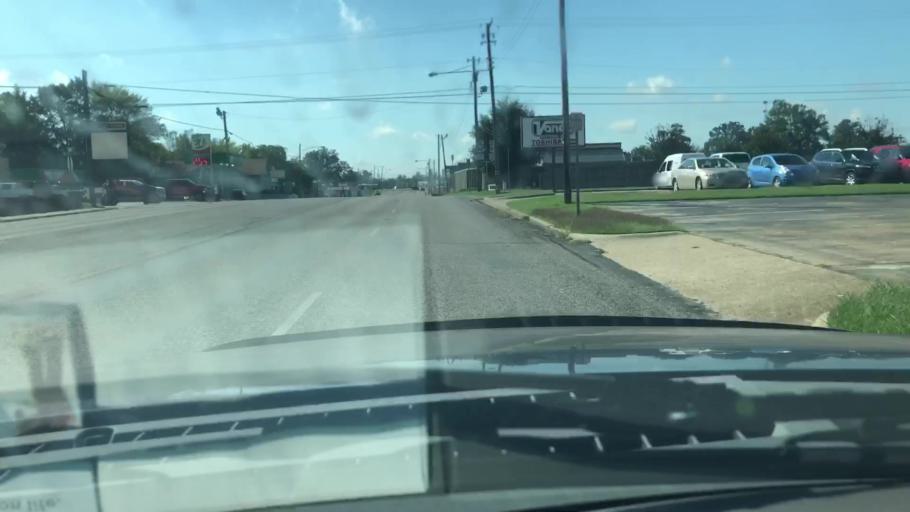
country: US
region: Texas
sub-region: Bowie County
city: Texarkana
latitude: 33.4391
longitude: -94.0533
